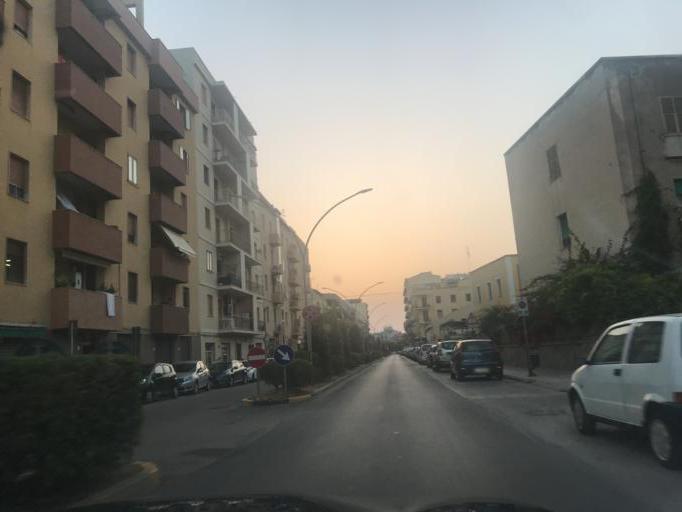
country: IT
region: Sardinia
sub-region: Provincia di Sassari
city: Alghero
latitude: 40.5538
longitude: 8.3226
